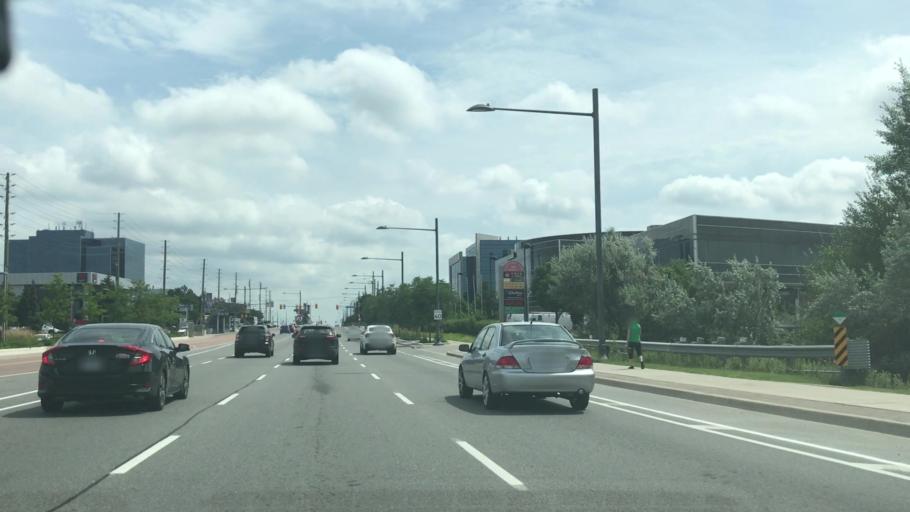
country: CA
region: Ontario
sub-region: York
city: Richmond Hill
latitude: 43.8427
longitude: -79.3891
